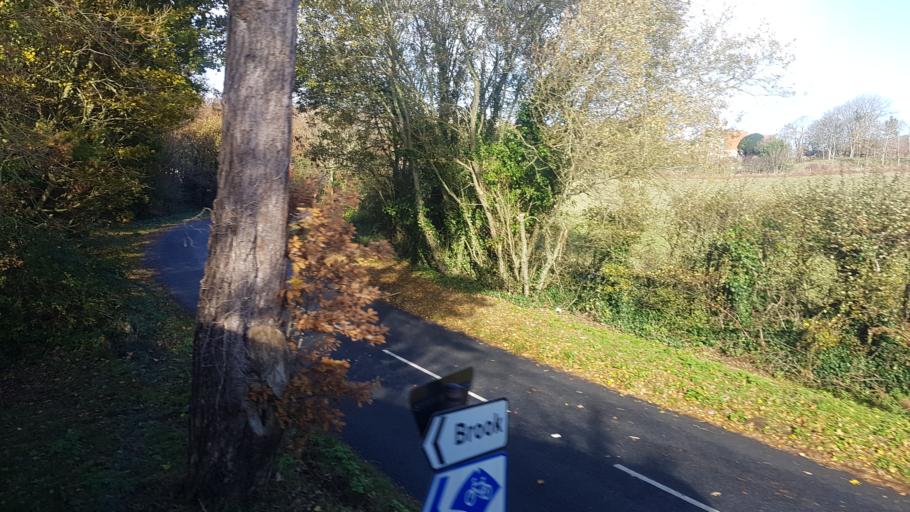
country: GB
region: England
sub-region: Isle of Wight
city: Shalfleet
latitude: 50.6560
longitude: -1.4433
